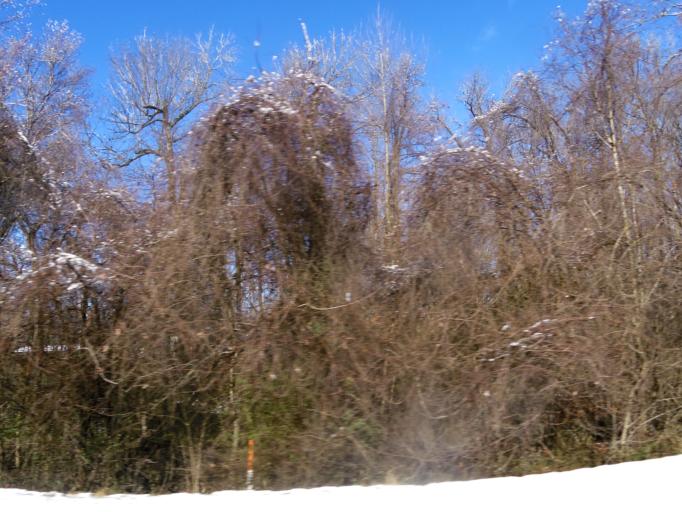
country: US
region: North Carolina
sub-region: Wilson County
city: Wilson
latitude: 35.7319
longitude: -77.8825
